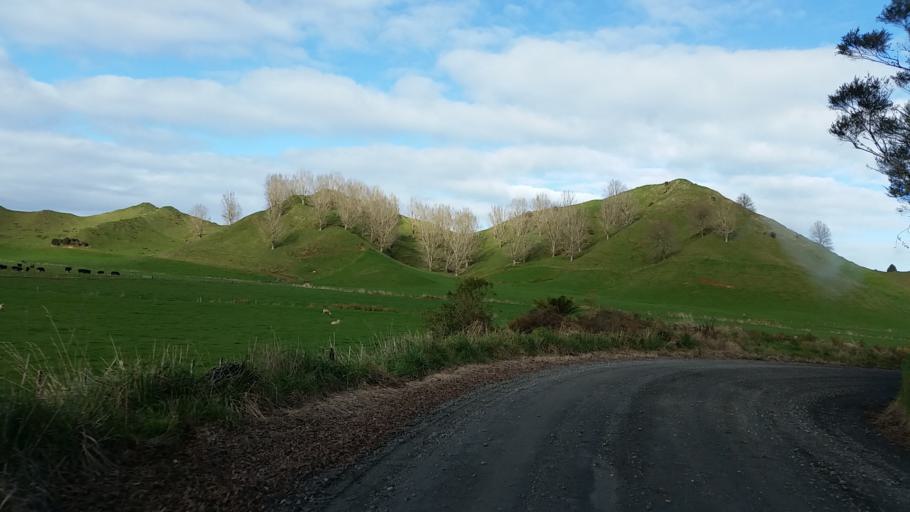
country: NZ
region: Taranaki
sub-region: South Taranaki District
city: Eltham
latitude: -39.2550
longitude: 174.5294
